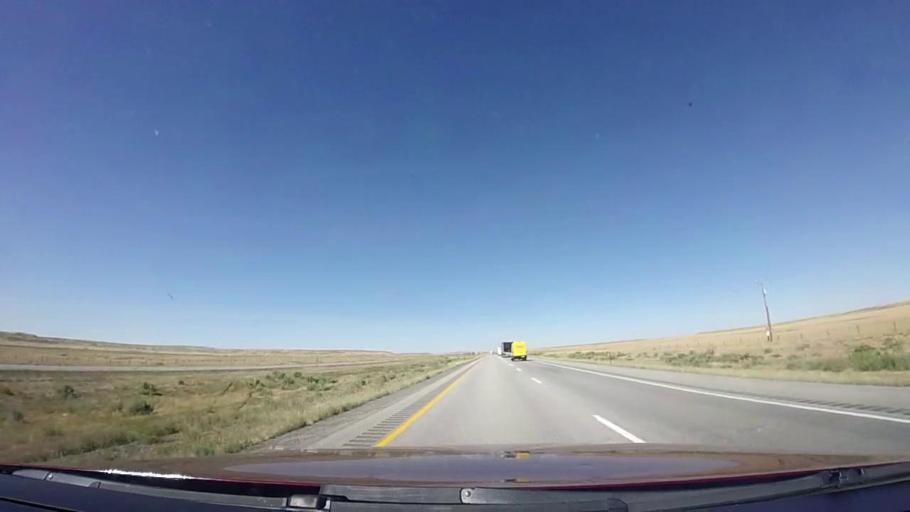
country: US
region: Wyoming
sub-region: Carbon County
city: Rawlins
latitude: 41.6634
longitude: -108.0476
